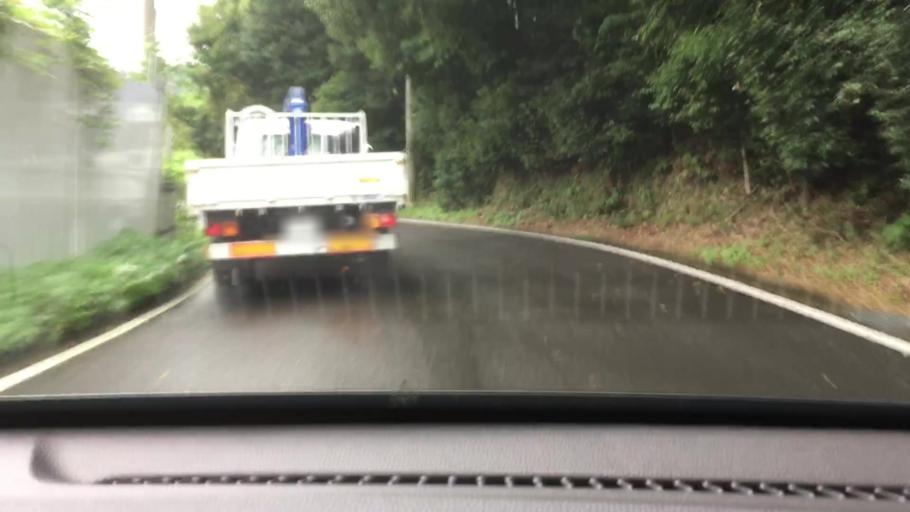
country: JP
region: Nagasaki
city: Togitsu
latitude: 32.8578
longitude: 129.7784
